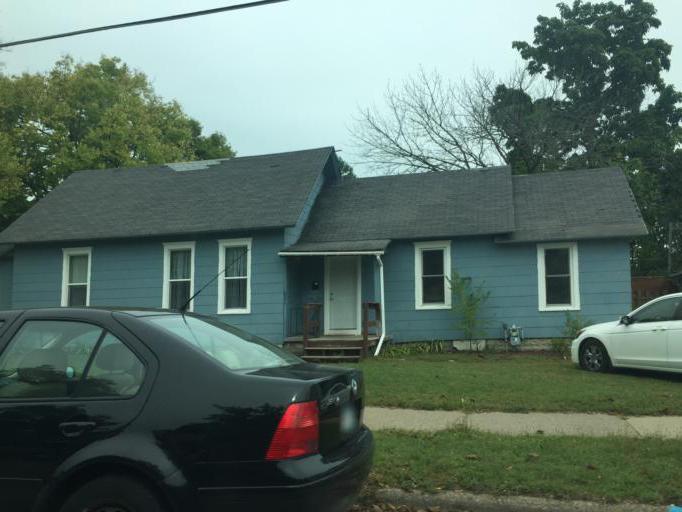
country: US
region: Minnesota
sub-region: Winona County
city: Winona
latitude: 44.0453
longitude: -91.6505
